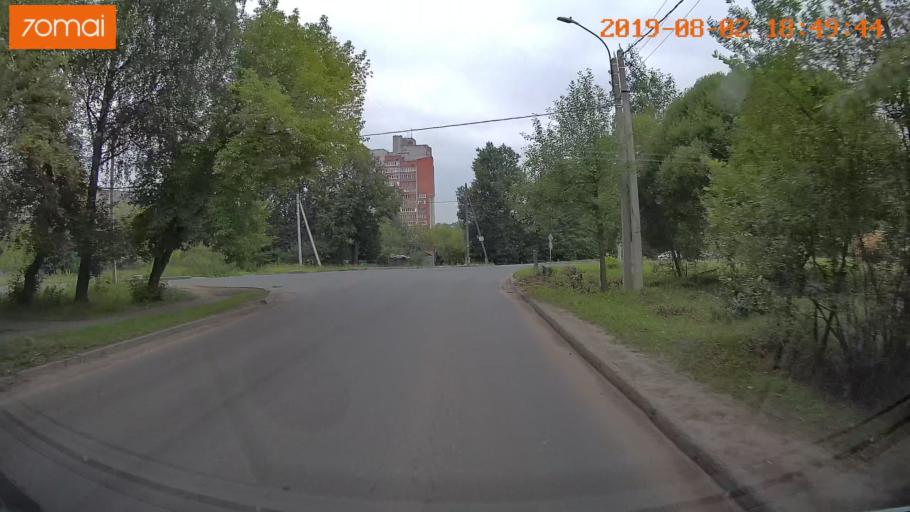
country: RU
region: Ivanovo
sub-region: Gorod Ivanovo
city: Ivanovo
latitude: 56.9895
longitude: 41.0214
